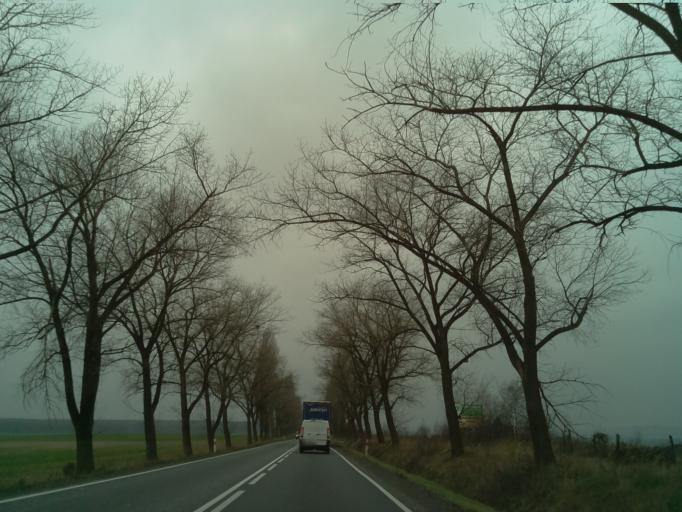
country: PL
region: Lower Silesian Voivodeship
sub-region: Powiat swidnicki
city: Stanowice
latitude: 50.9145
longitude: 16.3680
